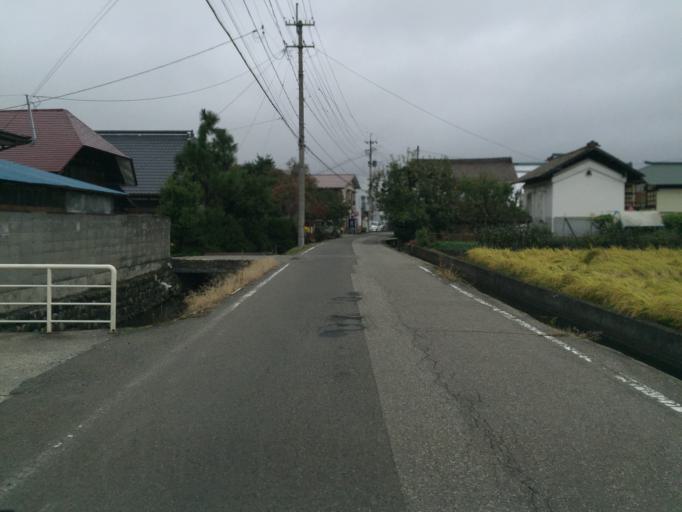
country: JP
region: Fukushima
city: Kitakata
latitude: 37.4681
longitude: 139.9146
